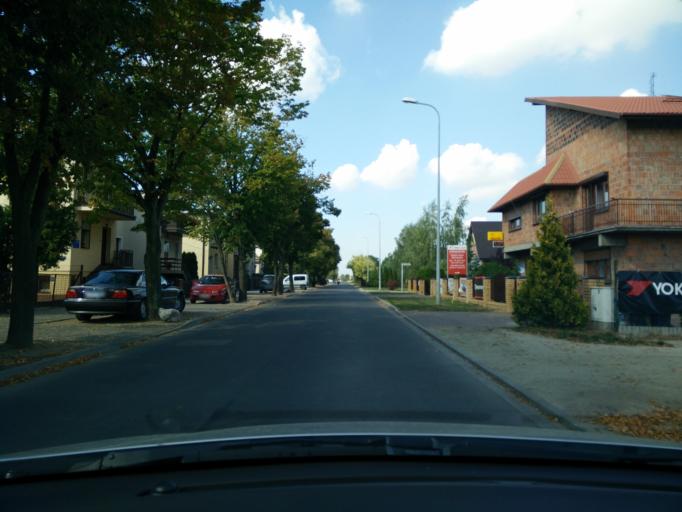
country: PL
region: Greater Poland Voivodeship
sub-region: Powiat sredzki
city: Sroda Wielkopolska
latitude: 52.2358
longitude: 17.2560
